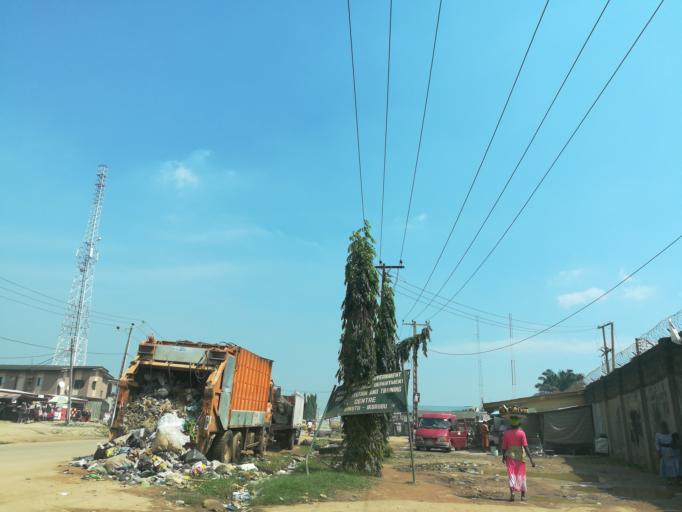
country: NG
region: Lagos
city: Ikorodu
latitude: 6.6398
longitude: 3.4812
